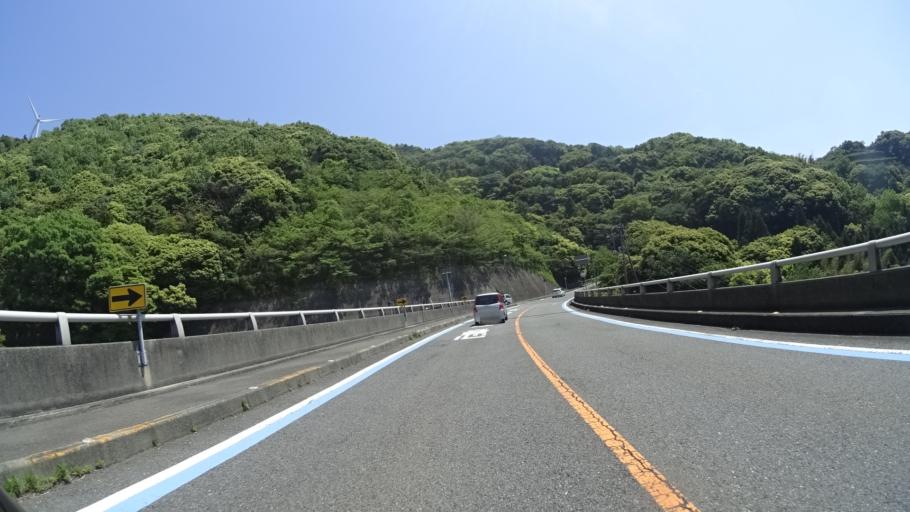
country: JP
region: Ehime
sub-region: Nishiuwa-gun
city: Ikata-cho
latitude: 33.4835
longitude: 132.3213
